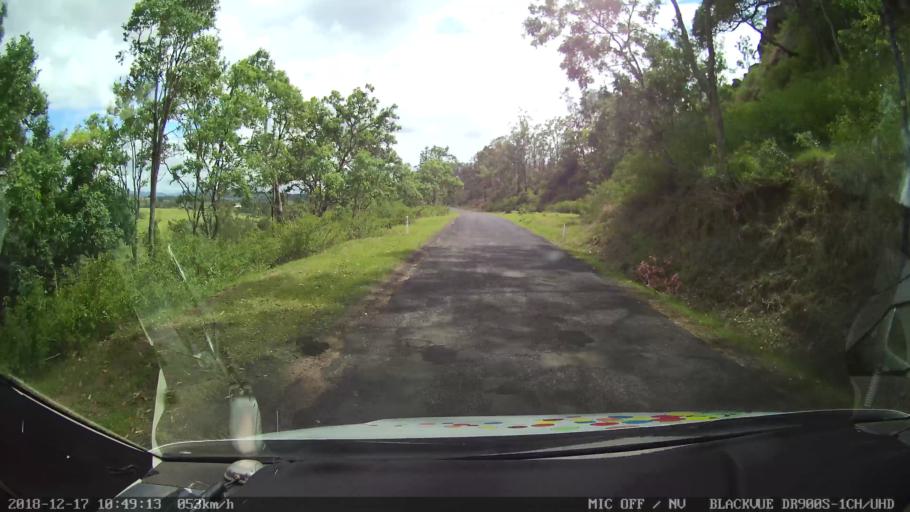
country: AU
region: New South Wales
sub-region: Clarence Valley
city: Gordon
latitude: -28.8673
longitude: 152.5726
